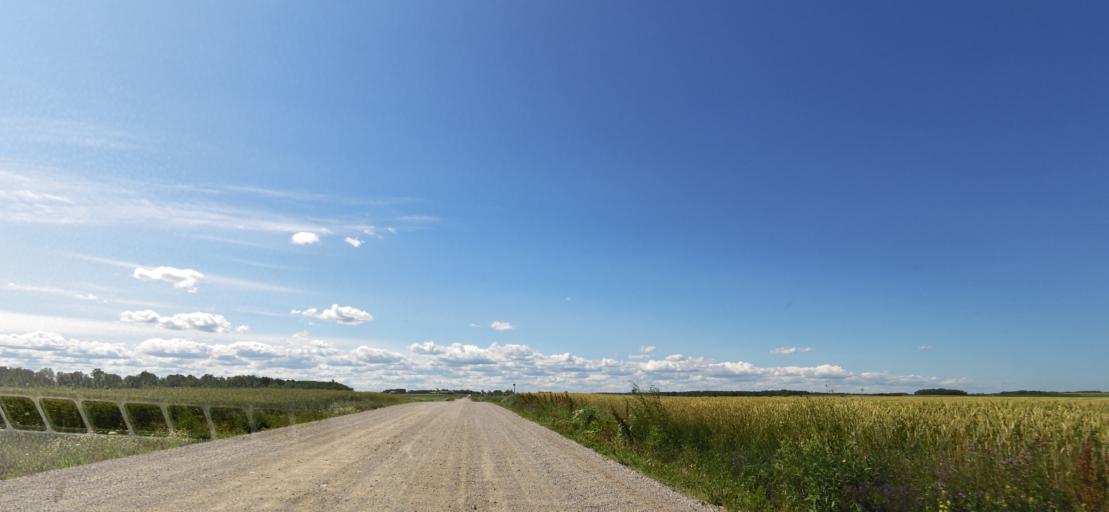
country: LT
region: Panevezys
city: Pasvalys
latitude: 56.2513
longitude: 24.3484
